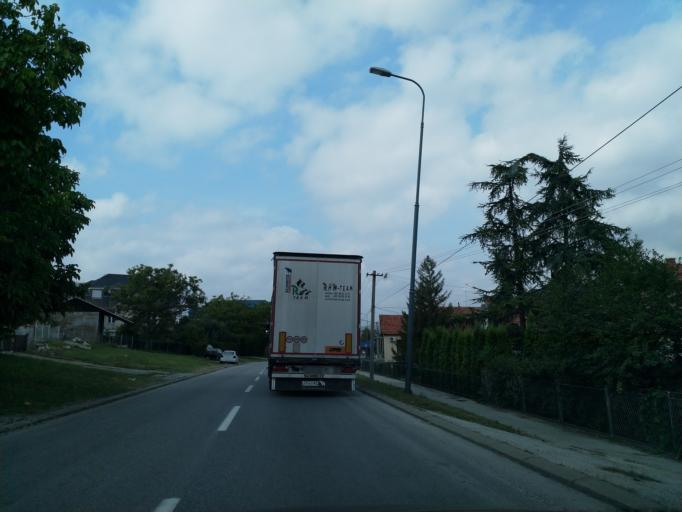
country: RS
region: Central Serbia
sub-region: Sumadijski Okrug
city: Kragujevac
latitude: 44.0325
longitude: 20.9141
